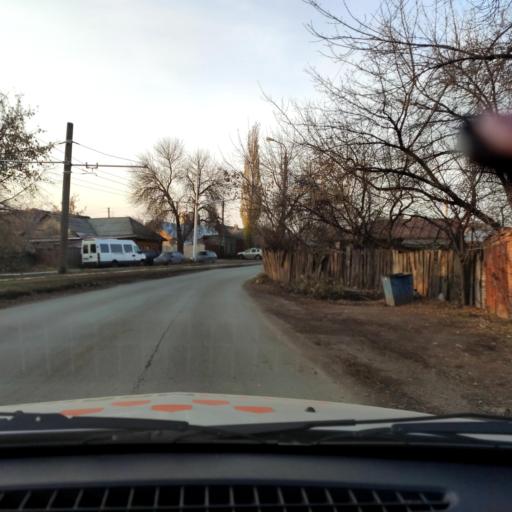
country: RU
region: Bashkortostan
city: Ufa
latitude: 54.7160
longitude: 55.9726
